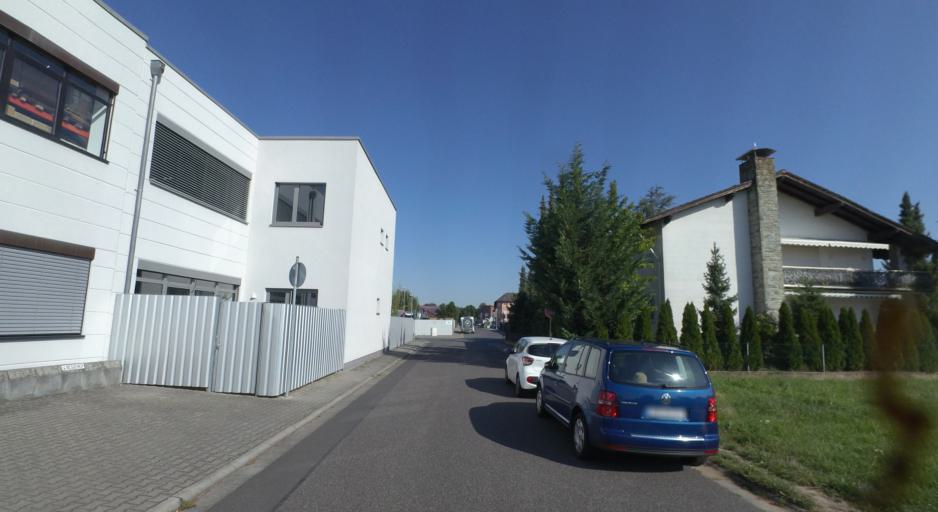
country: DE
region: Hesse
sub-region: Regierungsbezirk Darmstadt
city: Seligenstadt
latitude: 50.0186
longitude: 8.9952
